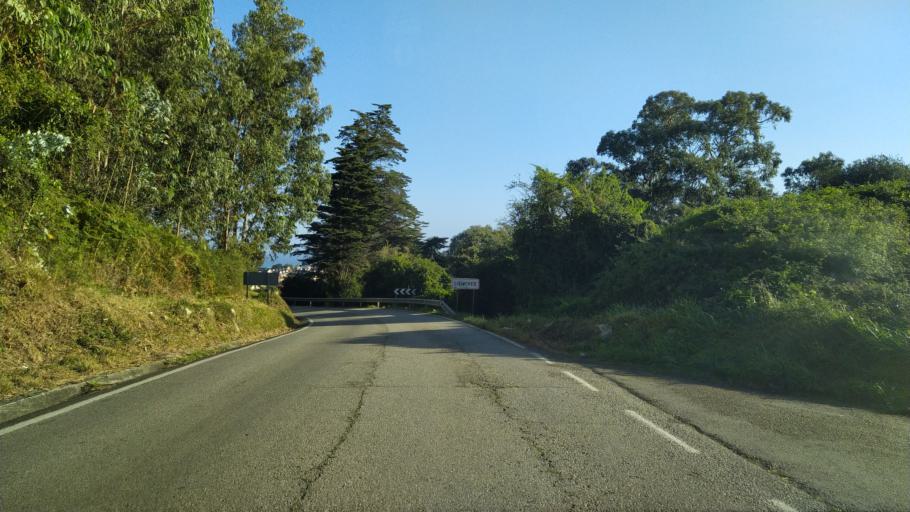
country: ES
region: Cantabria
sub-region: Provincia de Cantabria
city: Santa Cruz de Bezana
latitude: 43.4554
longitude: -3.9274
